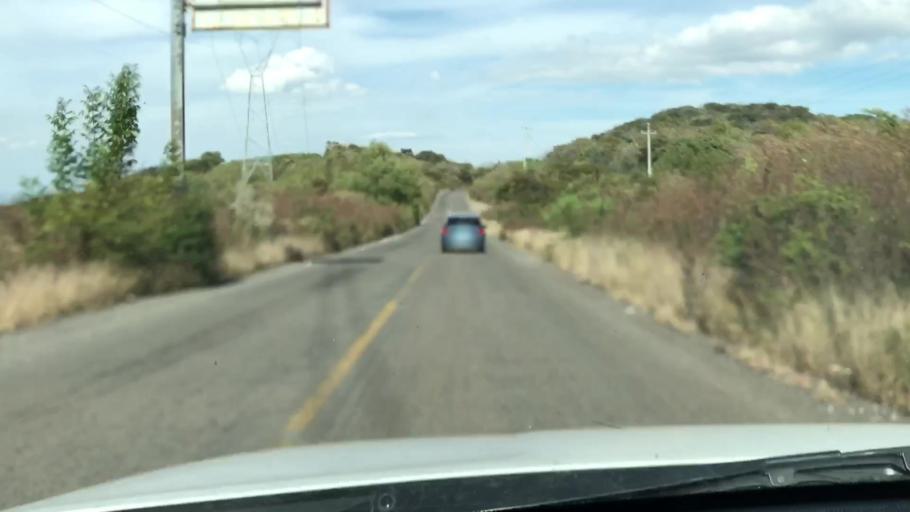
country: MX
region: Jalisco
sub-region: Zacoalco de Torres
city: Barranca de Otates (Barranca de Otatan)
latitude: 20.2229
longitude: -103.6916
